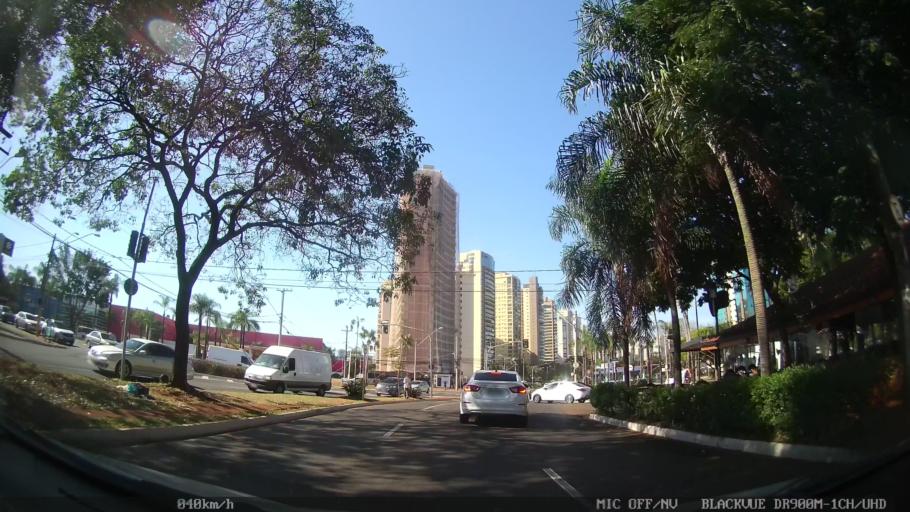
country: BR
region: Sao Paulo
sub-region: Ribeirao Preto
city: Ribeirao Preto
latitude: -21.2034
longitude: -47.8107
